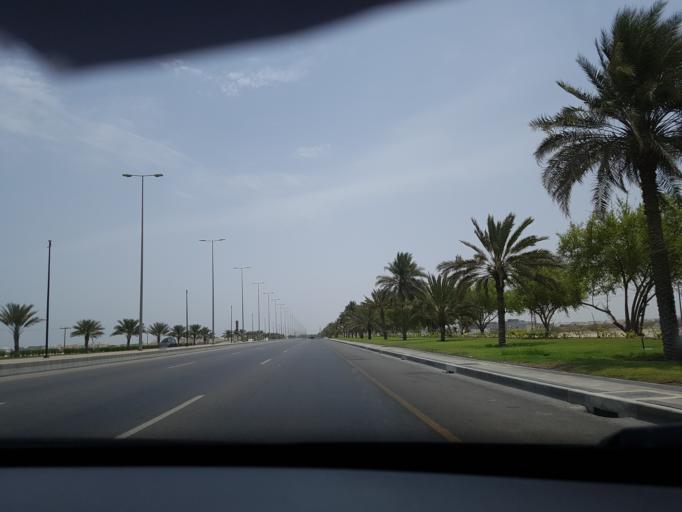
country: OM
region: Muhafazat Masqat
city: As Sib al Jadidah
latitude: 23.6853
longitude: 58.0964
